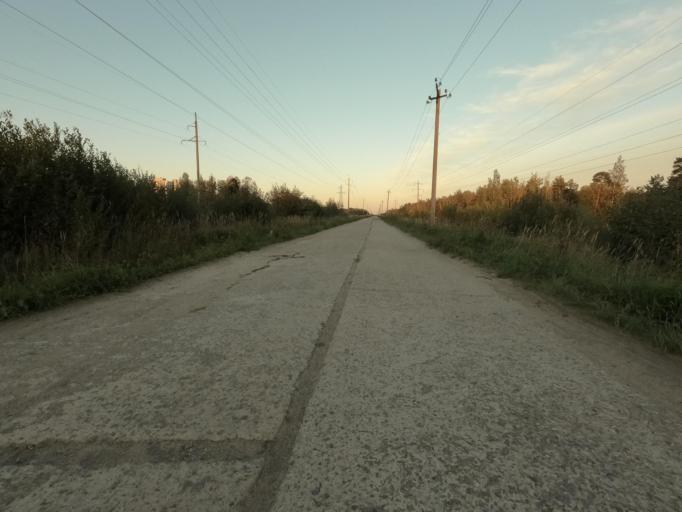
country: RU
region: Leningrad
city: Otradnoye
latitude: 59.7618
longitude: 30.7977
